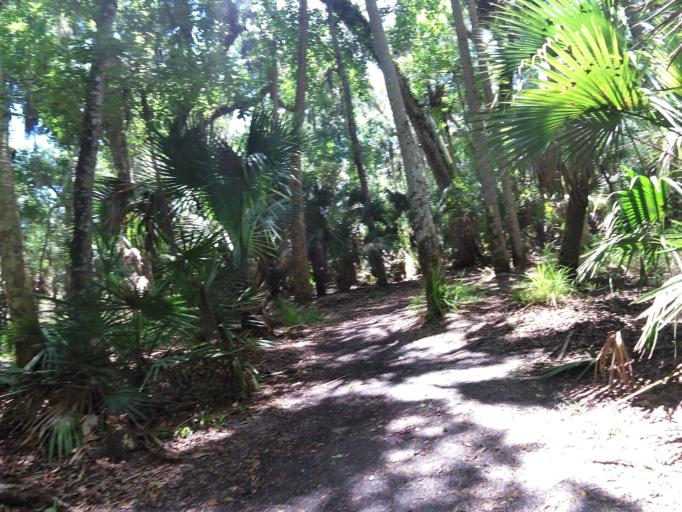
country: US
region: Florida
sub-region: Flagler County
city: Flagler Beach
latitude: 29.4287
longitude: -81.1411
